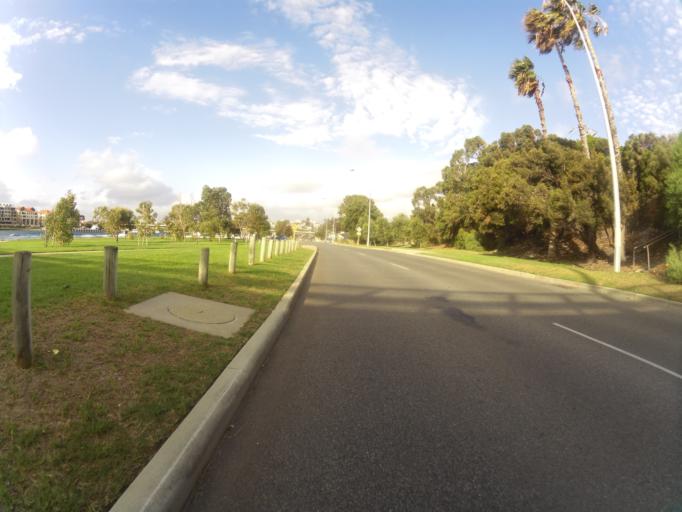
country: AU
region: Western Australia
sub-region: Fremantle
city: North Fremantle
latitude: -32.0423
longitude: 115.7549
